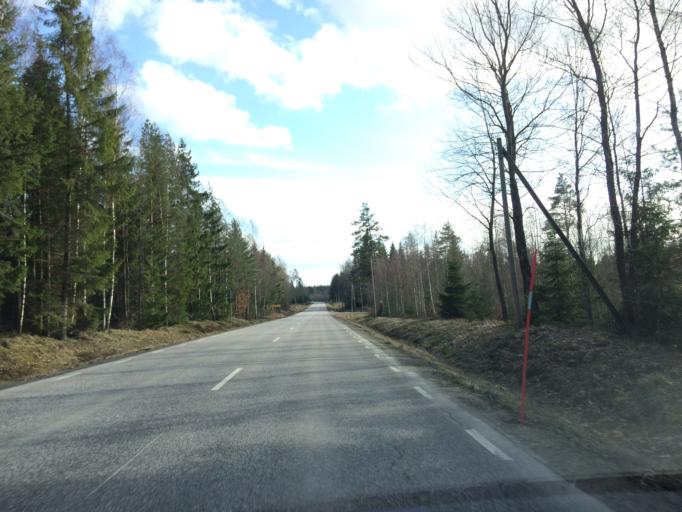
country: SE
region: Kronoberg
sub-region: Almhults Kommun
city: AElmhult
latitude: 56.5870
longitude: 14.0983
